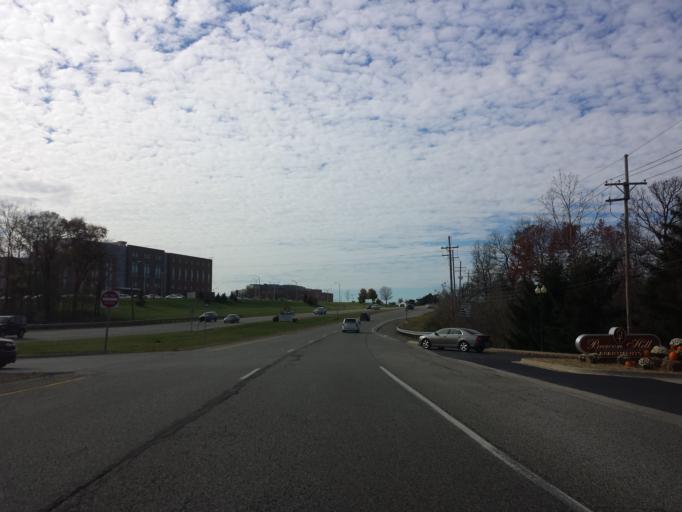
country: US
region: Michigan
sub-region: Oakland County
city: Auburn Hills
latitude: 42.6795
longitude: -83.2136
